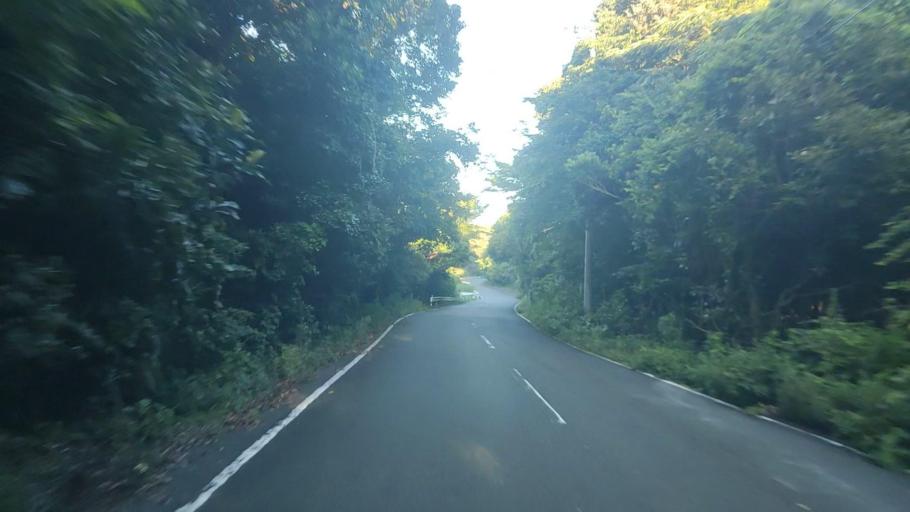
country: JP
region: Mie
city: Toba
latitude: 34.2640
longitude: 136.7718
